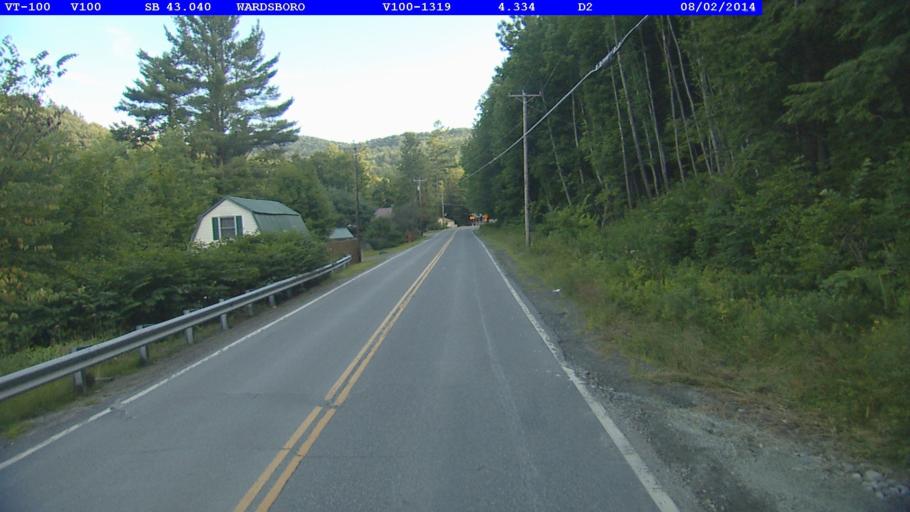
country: US
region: Vermont
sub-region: Windham County
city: Dover
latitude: 43.0270
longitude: -72.8199
